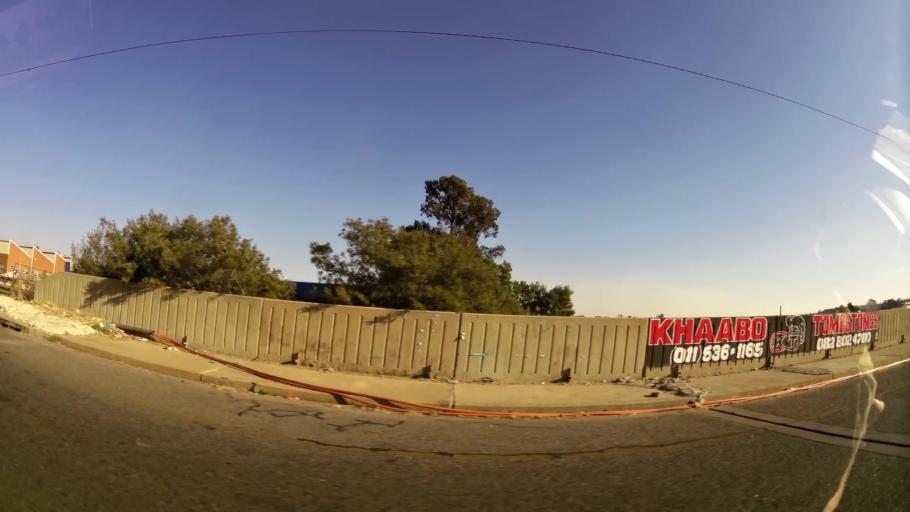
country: ZA
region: Gauteng
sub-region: City of Johannesburg Metropolitan Municipality
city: Johannesburg
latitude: -26.2043
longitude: 27.9531
